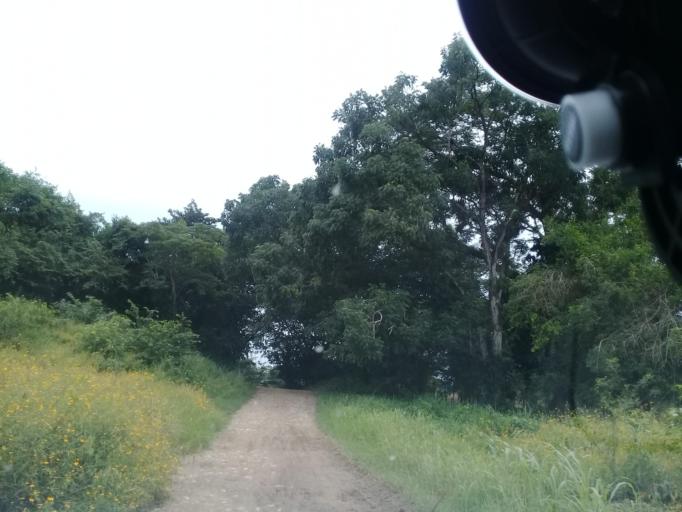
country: MX
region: Hidalgo
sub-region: Huejutla de Reyes
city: Chalahuiyapa
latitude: 21.1698
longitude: -98.3718
